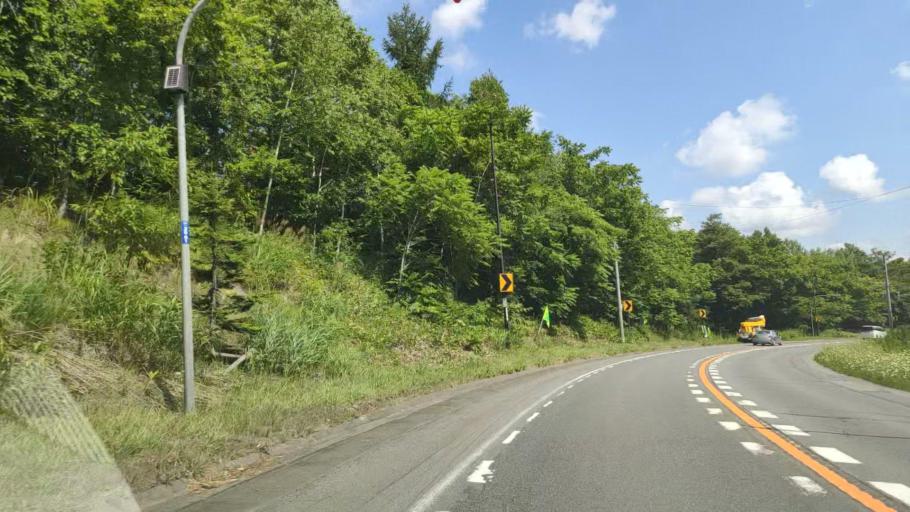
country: JP
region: Hokkaido
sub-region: Asahikawa-shi
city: Asahikawa
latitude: 43.5831
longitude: 142.4373
